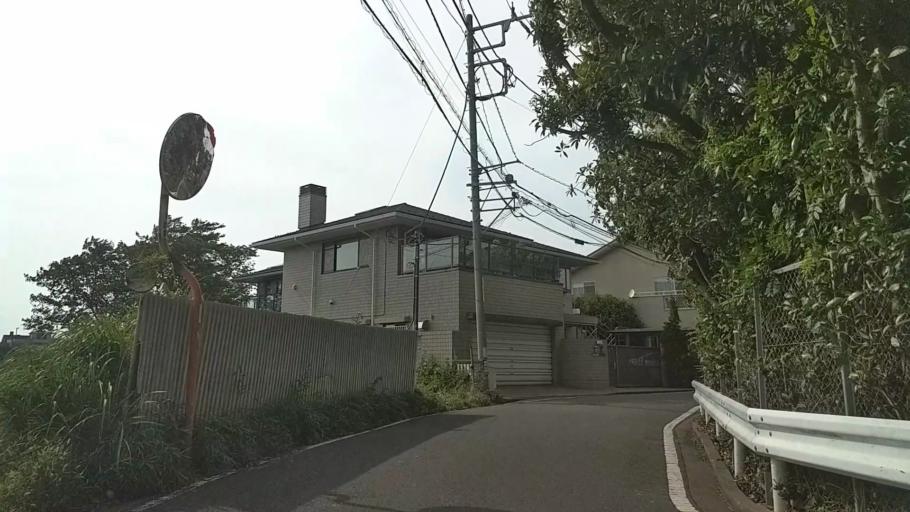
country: JP
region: Kanagawa
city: Yokohama
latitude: 35.4351
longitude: 139.6594
